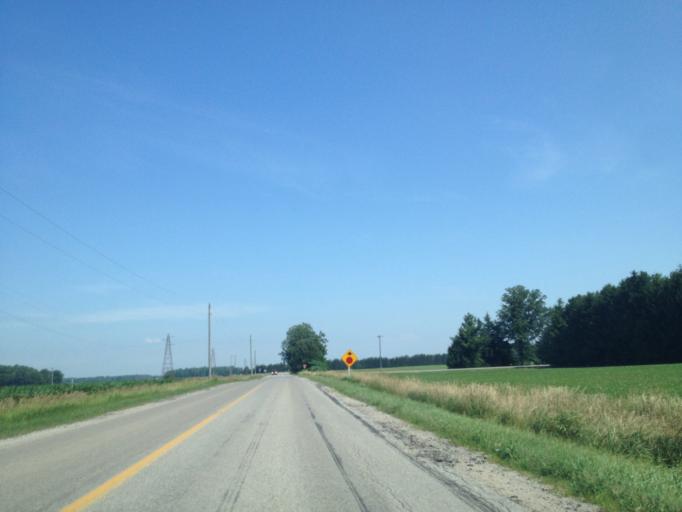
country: CA
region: Ontario
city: London
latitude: 43.0971
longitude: -81.2220
